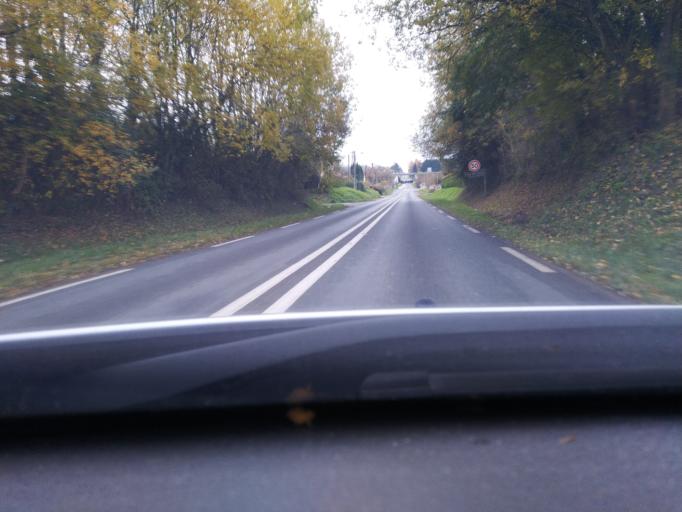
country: FR
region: Haute-Normandie
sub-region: Departement de la Seine-Maritime
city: La Vaupaliere
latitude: 49.4933
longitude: 0.9938
